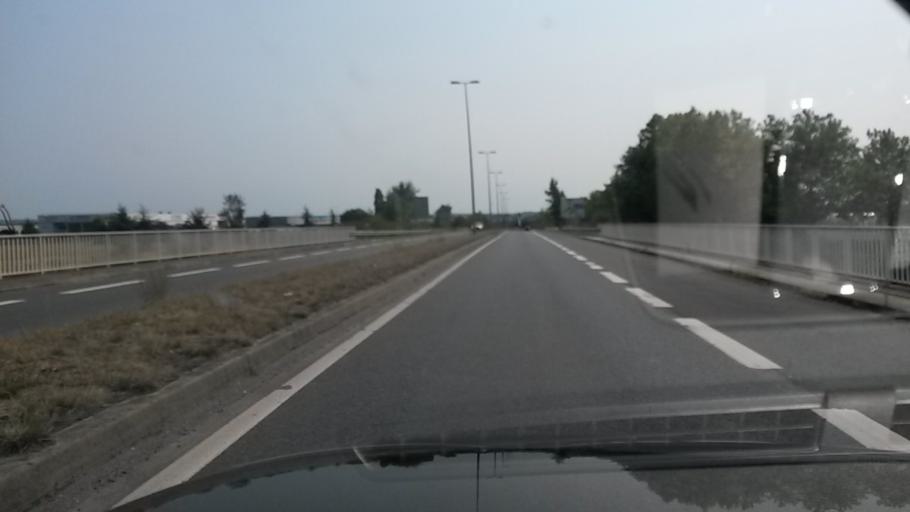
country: FR
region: Pays de la Loire
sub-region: Departement de la Loire-Atlantique
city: Saint-Gereon
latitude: 47.4022
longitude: -1.1910
